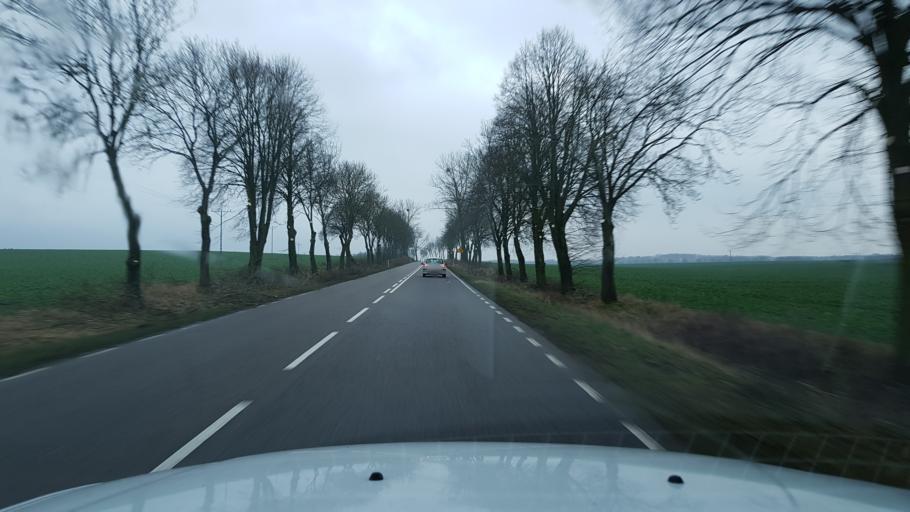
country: PL
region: West Pomeranian Voivodeship
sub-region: Powiat gryficki
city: Ploty
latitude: 53.8536
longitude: 15.2279
